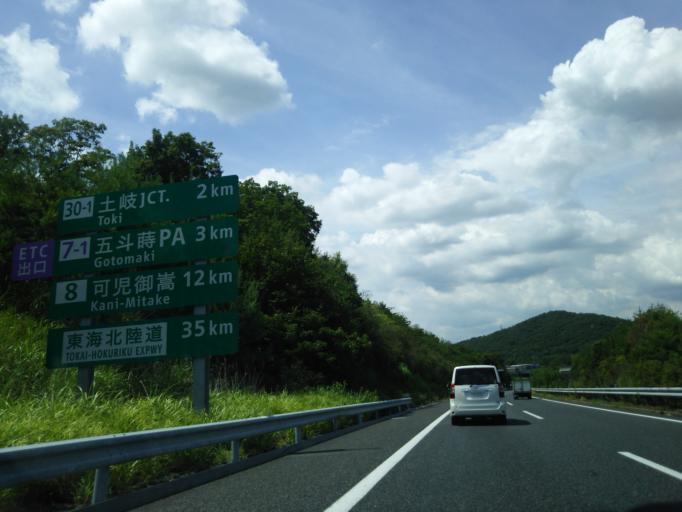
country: JP
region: Gifu
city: Toki
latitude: 35.3438
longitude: 137.1659
